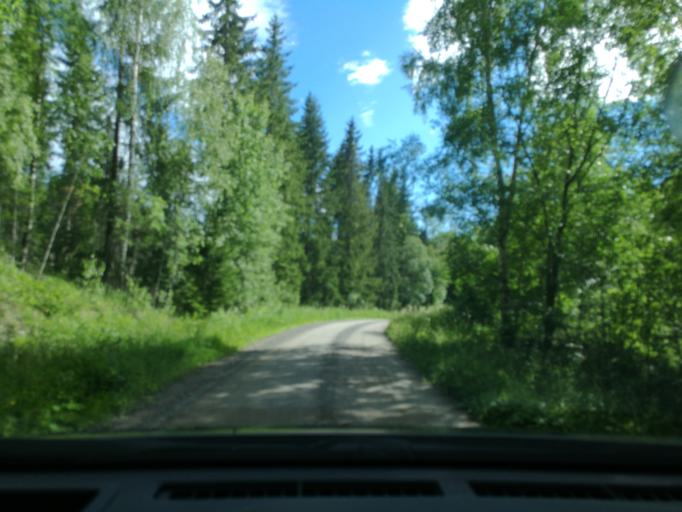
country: SE
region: Vaestmanland
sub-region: Surahammars Kommun
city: Ramnas
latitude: 59.7867
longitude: 16.3072
